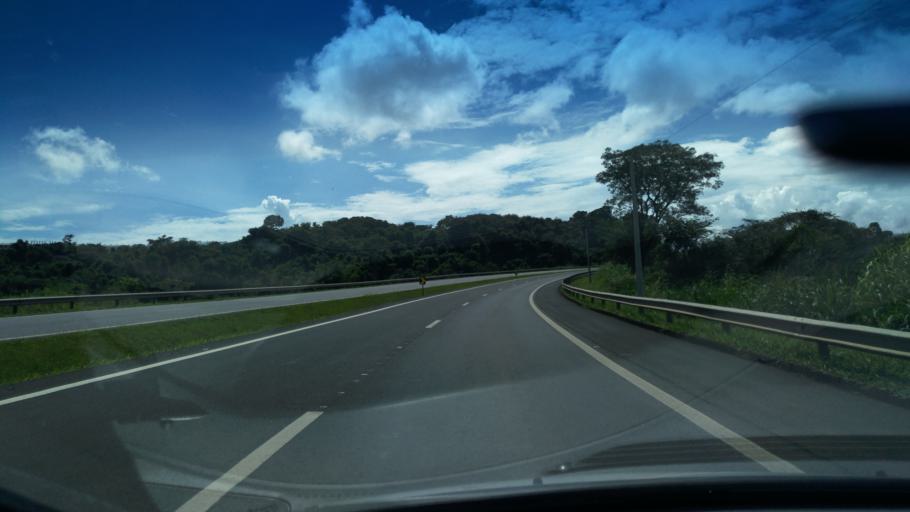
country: BR
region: Sao Paulo
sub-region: Santo Antonio Do Jardim
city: Espirito Santo do Pinhal
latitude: -22.2110
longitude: -46.7841
